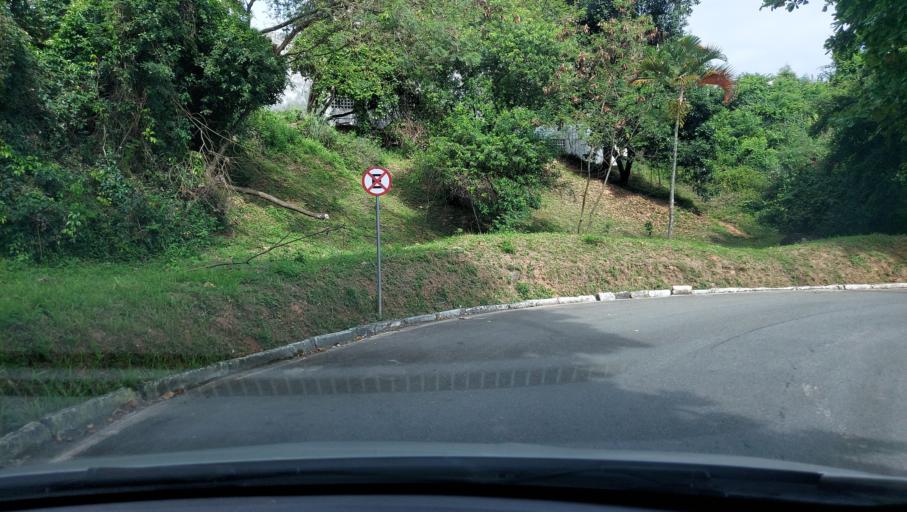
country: BR
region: Bahia
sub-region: Salvador
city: Salvador
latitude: -12.9818
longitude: -38.4610
